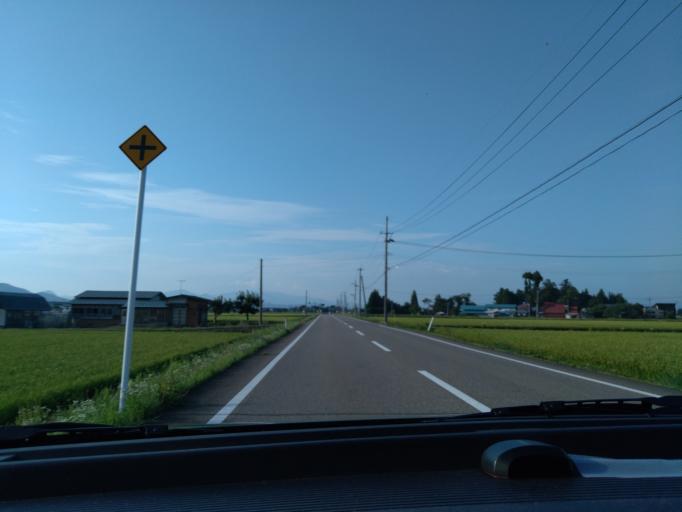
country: JP
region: Akita
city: Kakunodatemachi
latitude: 39.5127
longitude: 140.5588
